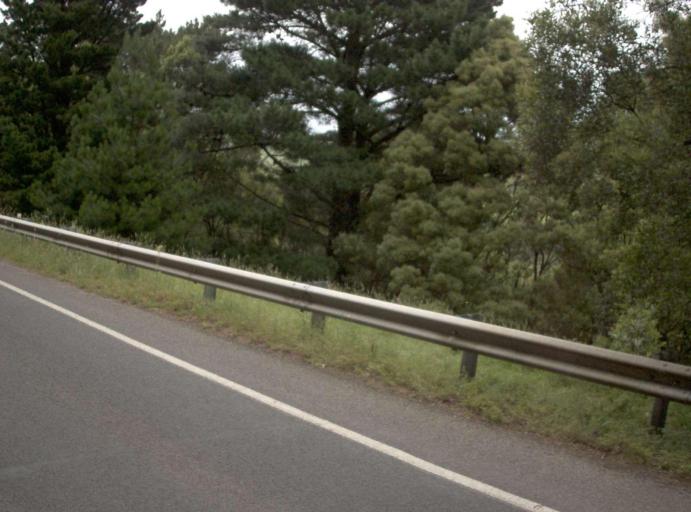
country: AU
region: Victoria
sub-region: Latrobe
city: Morwell
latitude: -38.6267
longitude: 146.1798
